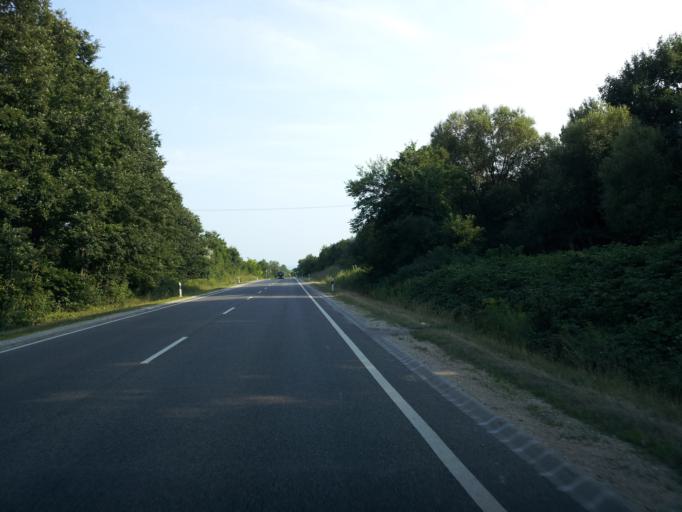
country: HU
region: Veszprem
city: Liter
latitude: 47.0811
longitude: 18.0352
